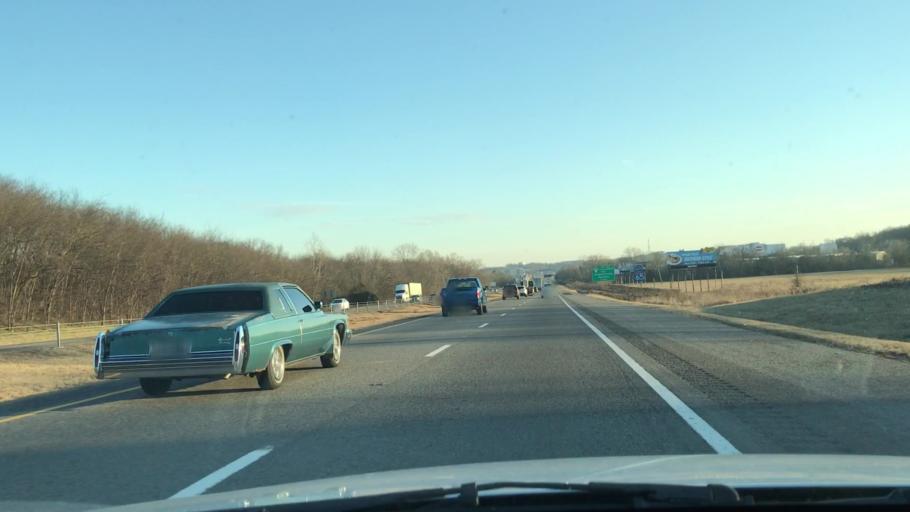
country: US
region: Tennessee
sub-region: Davidson County
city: Goodlettsville
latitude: 36.3407
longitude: -86.7134
